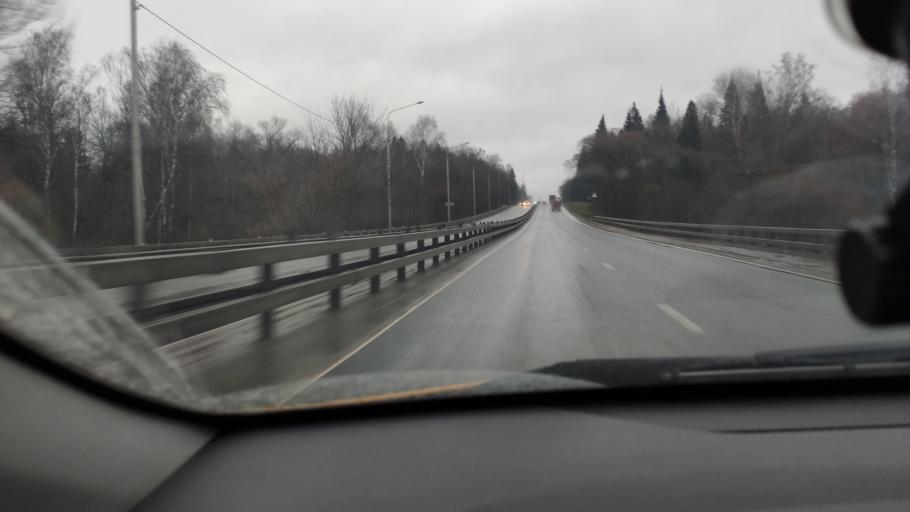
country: RU
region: Moskovskaya
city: Troitsk
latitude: 55.3409
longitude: 37.3098
